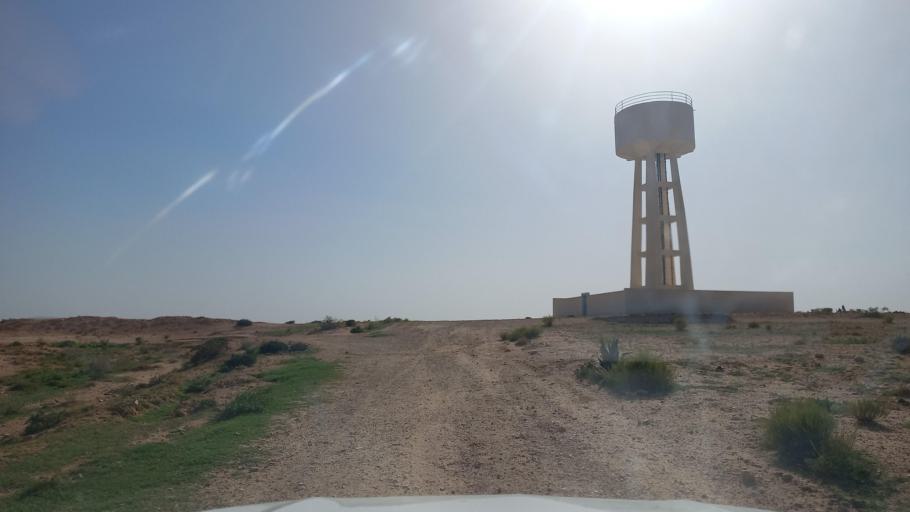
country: TN
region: Al Qasrayn
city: Kasserine
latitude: 35.3134
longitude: 9.0206
